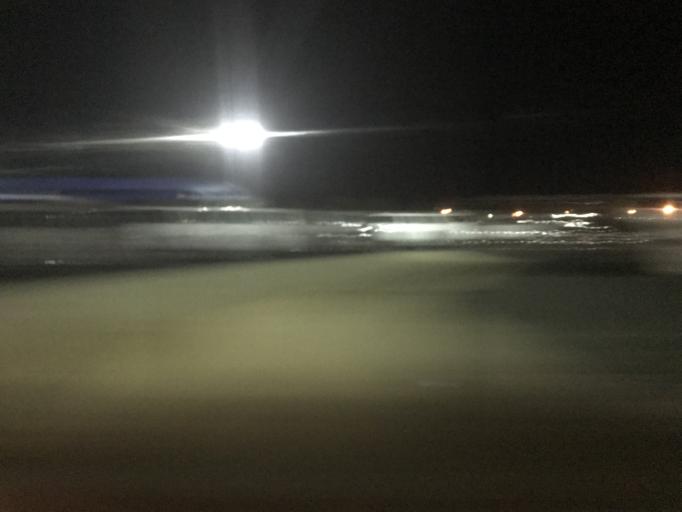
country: US
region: Texas
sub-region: Jones County
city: Anson
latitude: 32.7460
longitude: -99.8969
